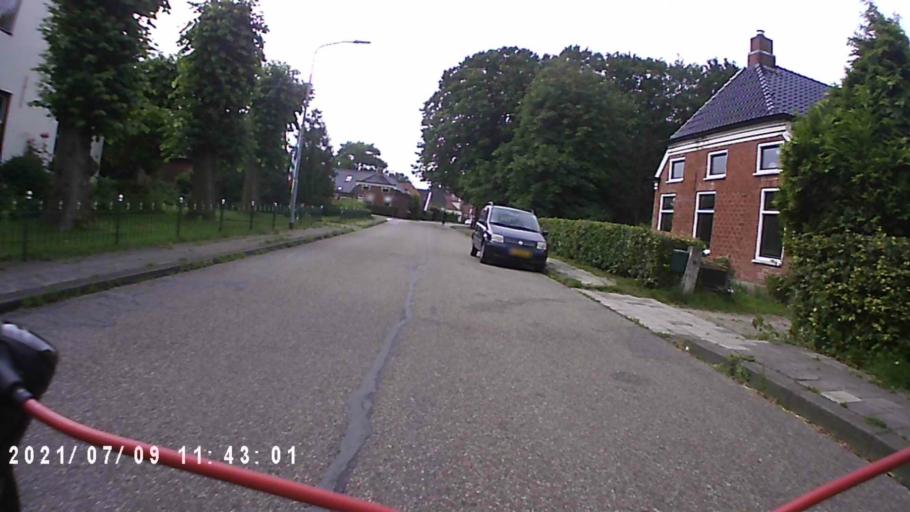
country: NL
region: Groningen
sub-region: Gemeente Slochteren
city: Slochteren
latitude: 53.2035
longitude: 6.8730
